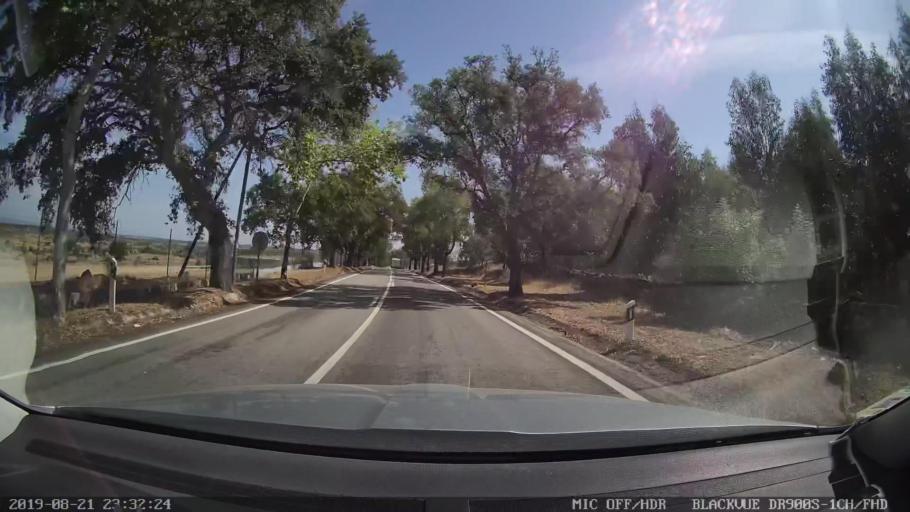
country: PT
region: Guarda
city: Alcains
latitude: 39.8781
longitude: -7.4134
